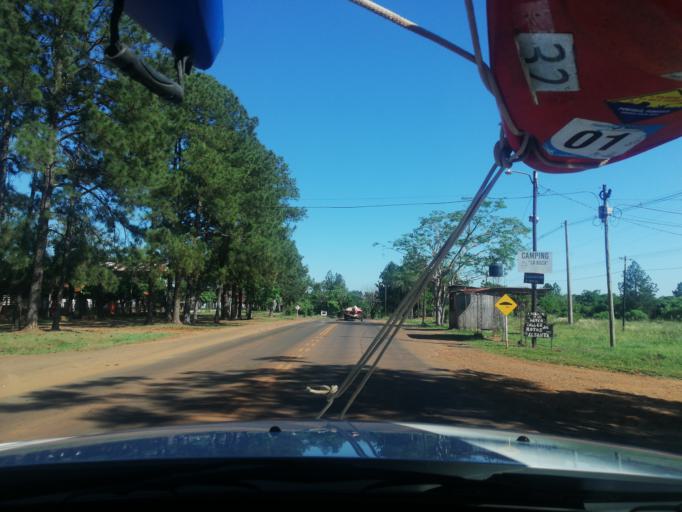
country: AR
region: Misiones
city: Santa Ana
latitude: -27.3637
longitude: -55.5859
